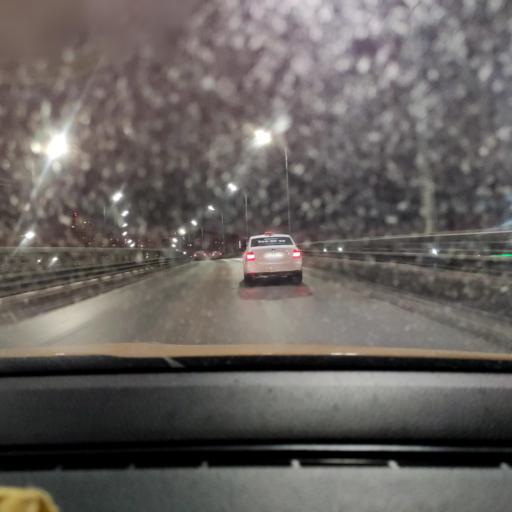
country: RU
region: Moskovskaya
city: Odintsovo
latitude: 55.6709
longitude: 37.2755
